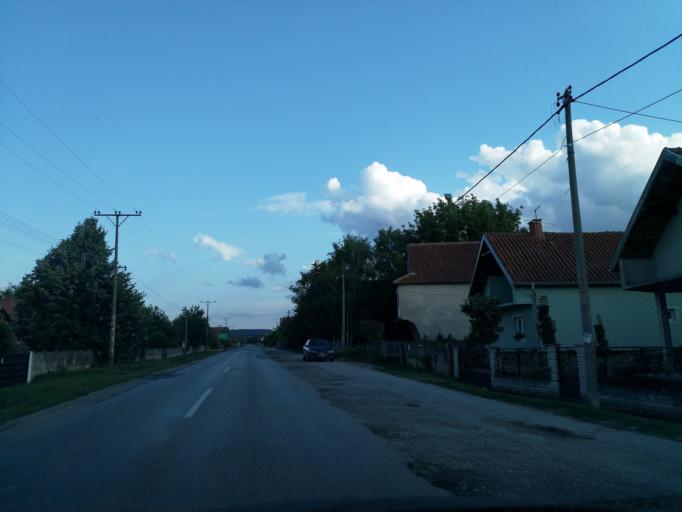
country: RS
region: Central Serbia
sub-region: Rasinski Okrug
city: Cicevac
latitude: 43.7629
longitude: 21.4303
